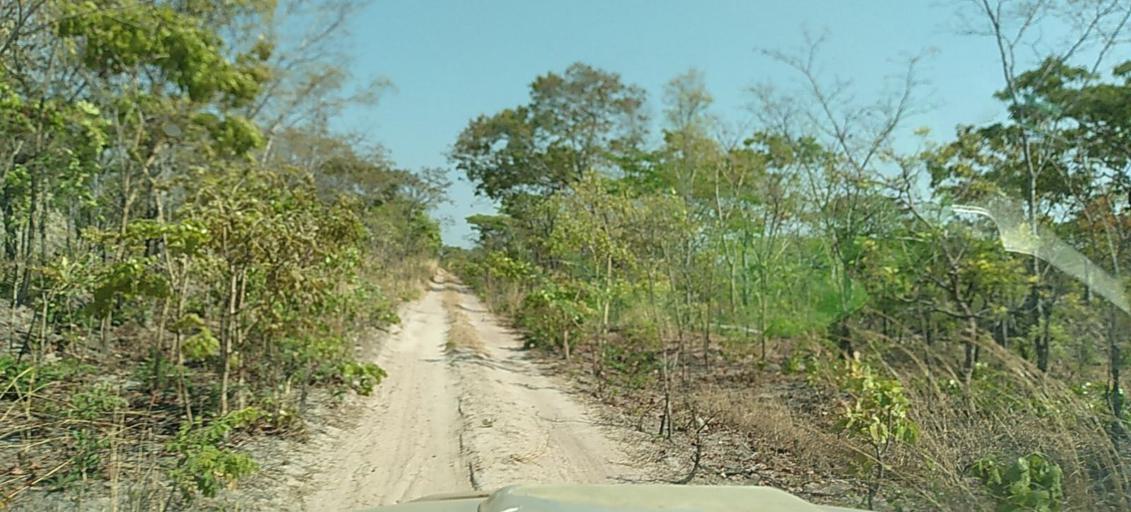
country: ZM
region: North-Western
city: Kalengwa
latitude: -13.3252
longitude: 24.8273
